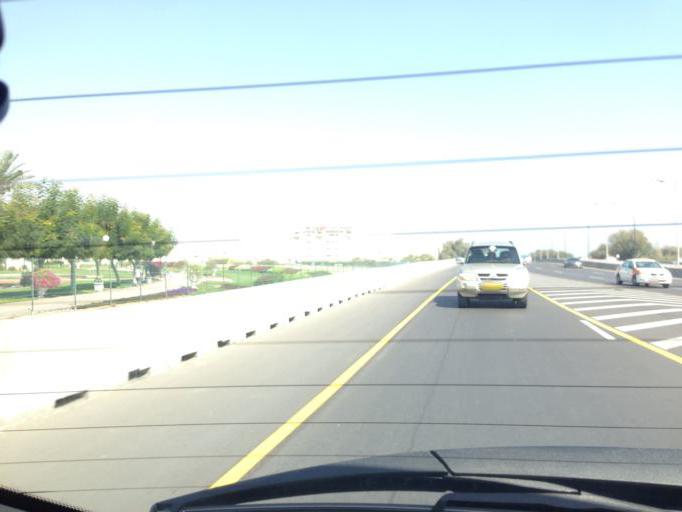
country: OM
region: Muhafazat Masqat
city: As Sib al Jadidah
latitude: 23.5925
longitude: 58.2510
